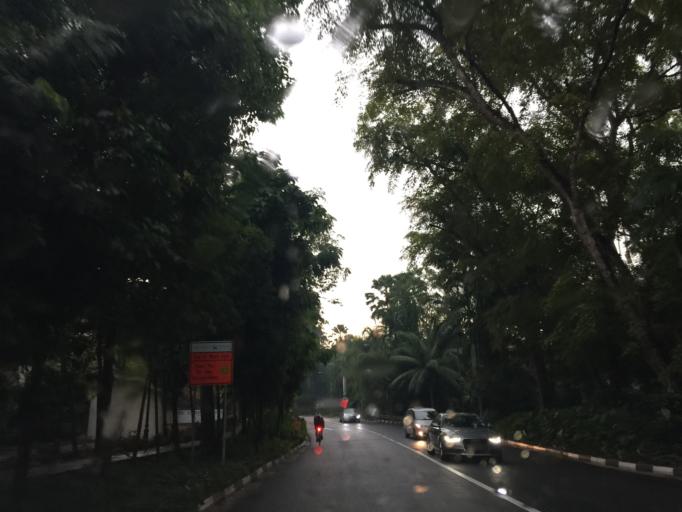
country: SG
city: Singapore
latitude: 1.3085
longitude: 103.8185
